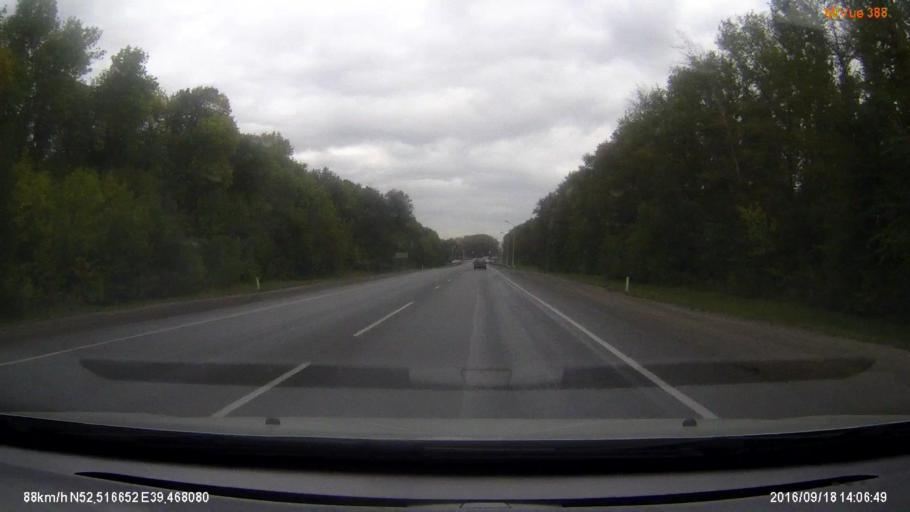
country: RU
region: Lipetsk
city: Syrskoye
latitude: 52.5889
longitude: 39.5256
